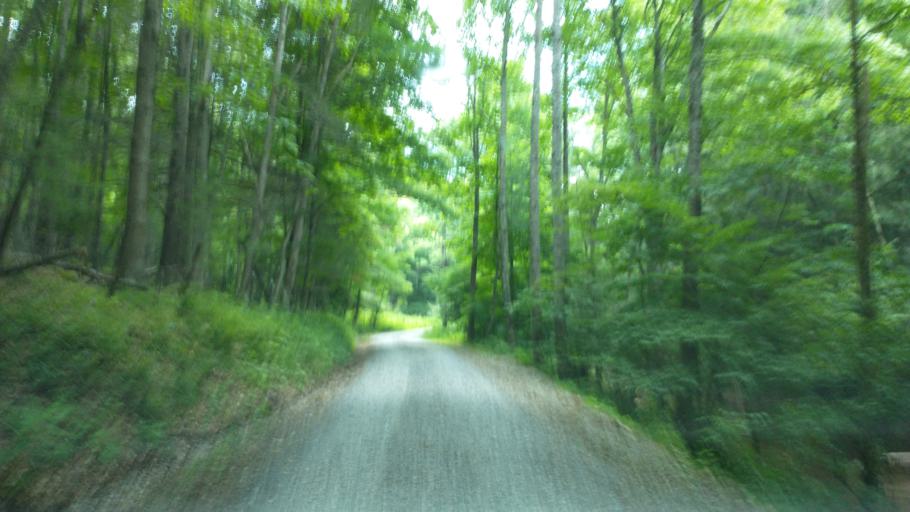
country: US
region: West Virginia
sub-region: Mercer County
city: Athens
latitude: 37.4317
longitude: -80.9980
